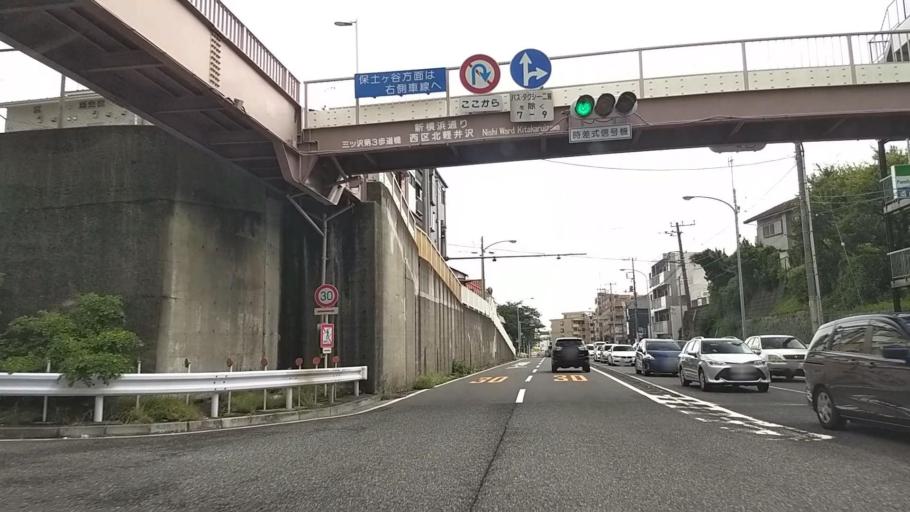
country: JP
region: Kanagawa
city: Yokohama
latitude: 35.4705
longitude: 139.6070
